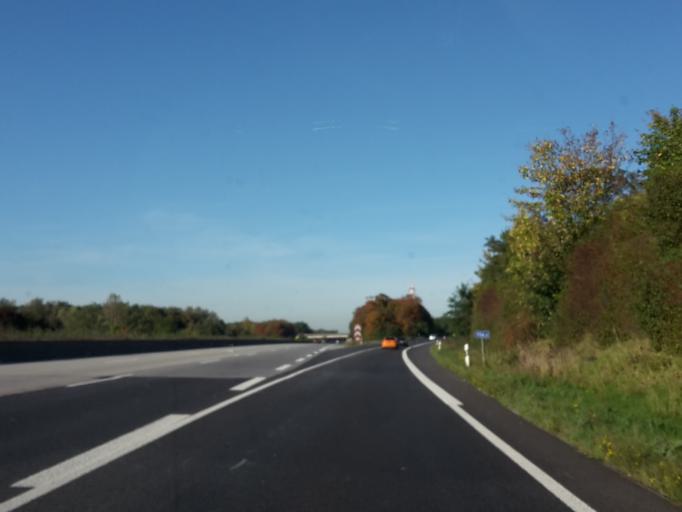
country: DE
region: Hesse
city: Viernheim
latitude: 49.5472
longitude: 8.5591
